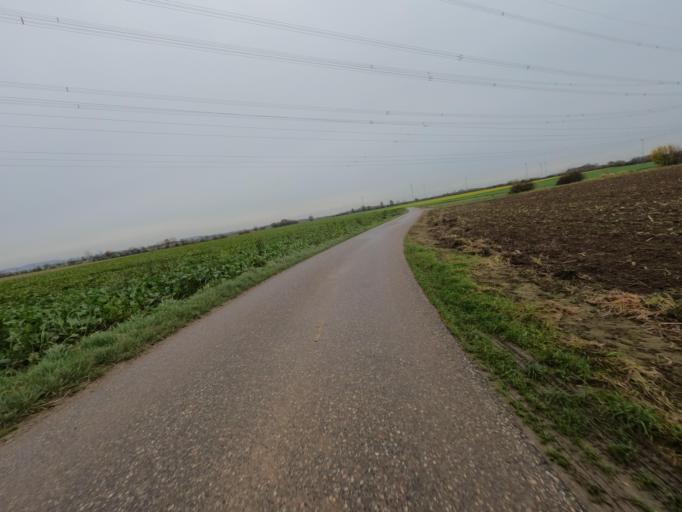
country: DE
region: North Rhine-Westphalia
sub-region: Regierungsbezirk Koln
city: Heinsberg
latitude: 51.0280
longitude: 6.1186
